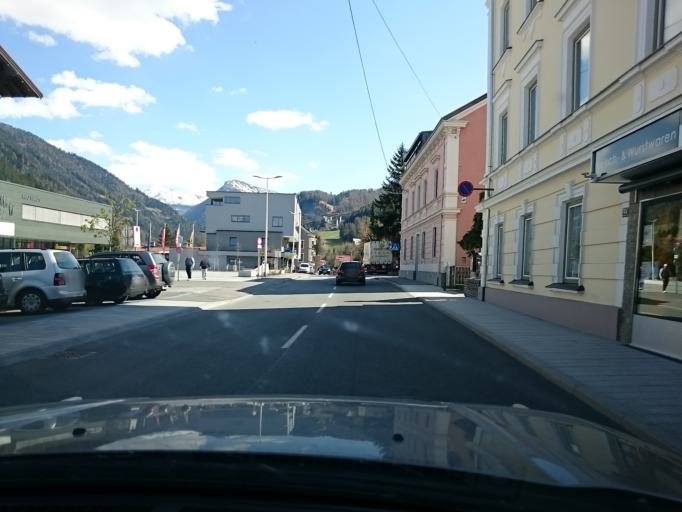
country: AT
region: Tyrol
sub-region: Politischer Bezirk Innsbruck Land
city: Steinach am Brenner
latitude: 47.0906
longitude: 11.4669
